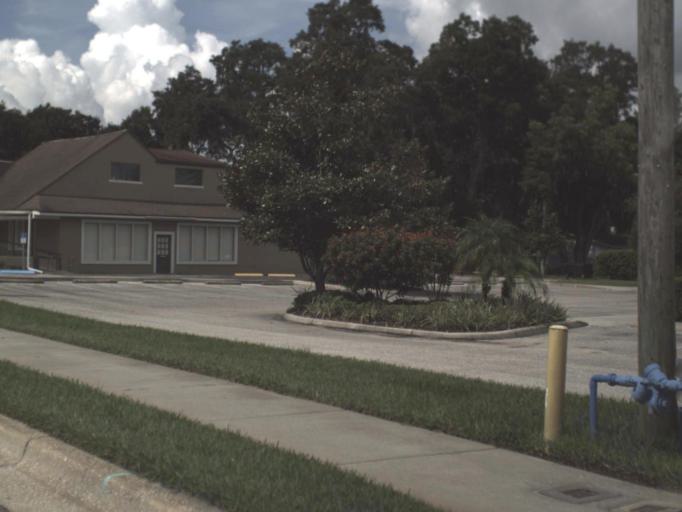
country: US
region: Florida
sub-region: Hillsborough County
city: Plant City
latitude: 28.0002
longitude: -82.1215
